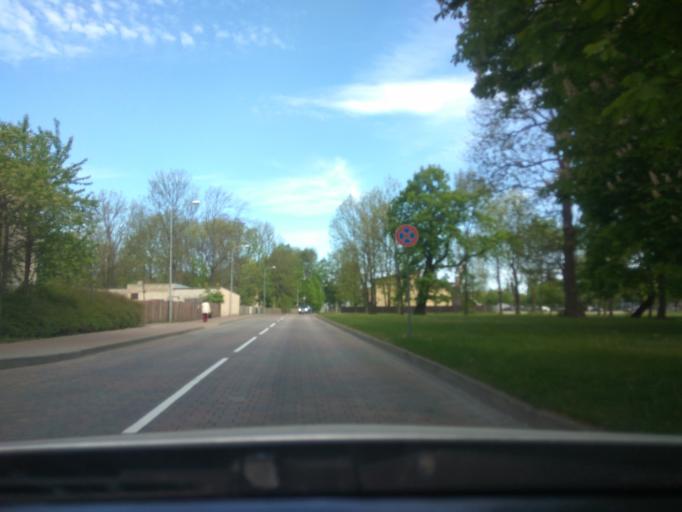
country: LV
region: Ventspils
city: Ventspils
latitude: 57.3955
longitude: 21.5716
